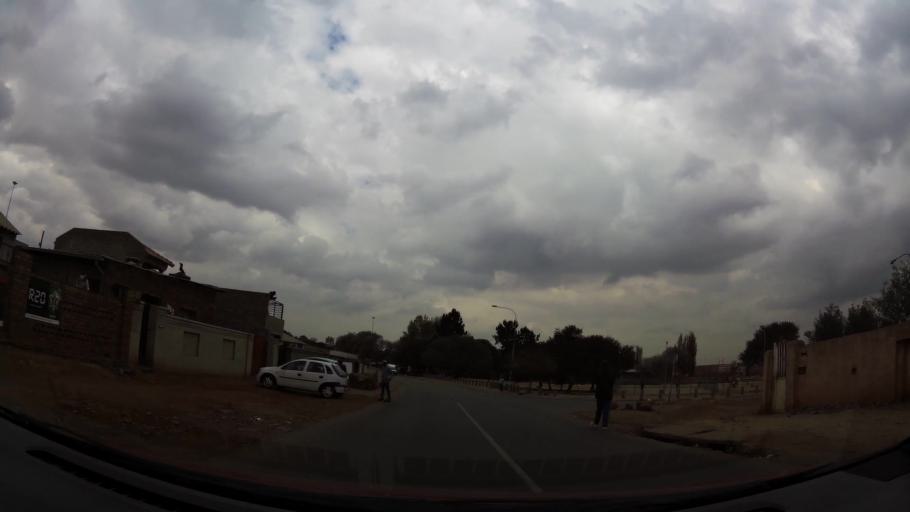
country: ZA
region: Gauteng
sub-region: City of Johannesburg Metropolitan Municipality
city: Soweto
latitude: -26.2594
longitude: 27.8436
